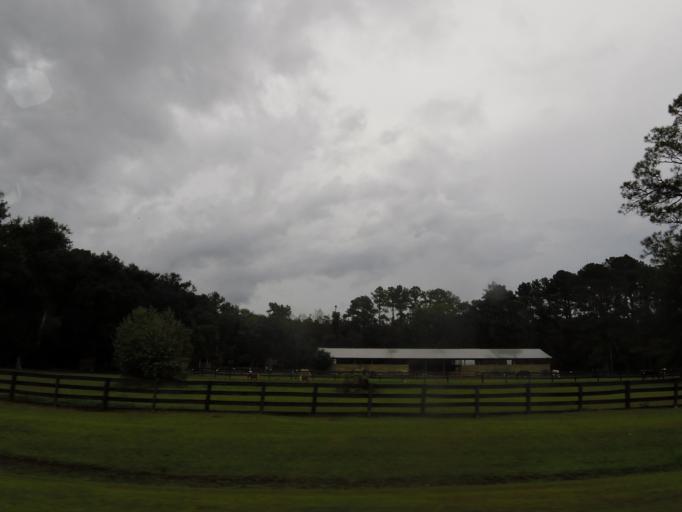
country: US
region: Georgia
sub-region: Wayne County
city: Jesup
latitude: 31.5548
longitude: -81.8195
